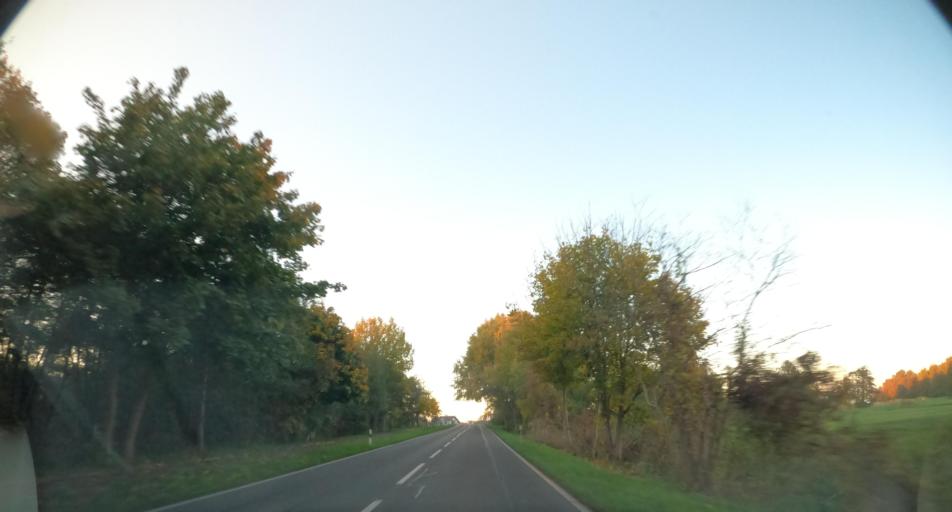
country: DE
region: Mecklenburg-Vorpommern
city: Ueckermunde
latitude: 53.7520
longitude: 14.0251
